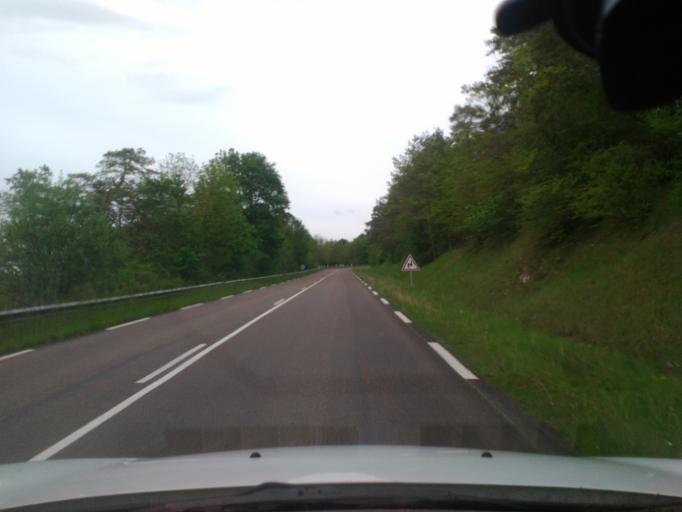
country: FR
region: Champagne-Ardenne
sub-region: Departement de l'Aube
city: Bar-sur-Aube
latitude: 48.2250
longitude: 4.7525
